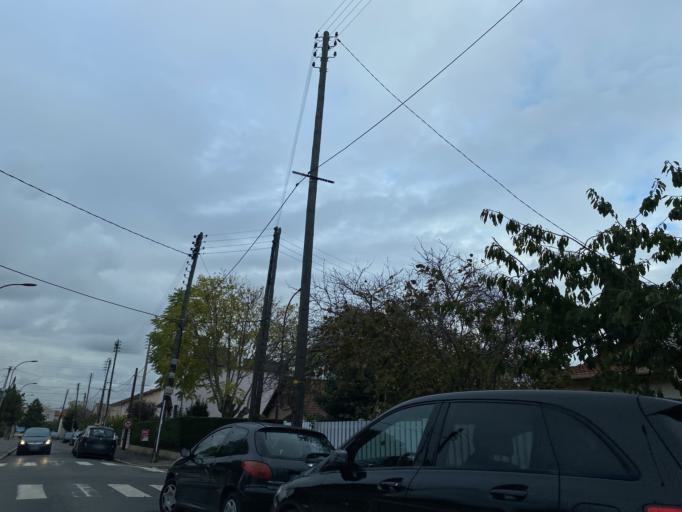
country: FR
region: Ile-de-France
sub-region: Departement du Val-d'Oise
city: Bezons
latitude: 48.9276
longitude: 2.2038
